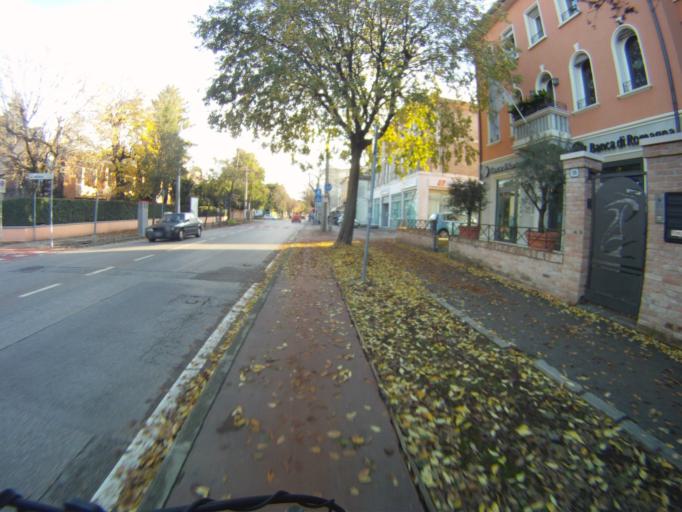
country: IT
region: Veneto
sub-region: Provincia di Padova
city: Padova
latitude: 45.3981
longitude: 11.8868
